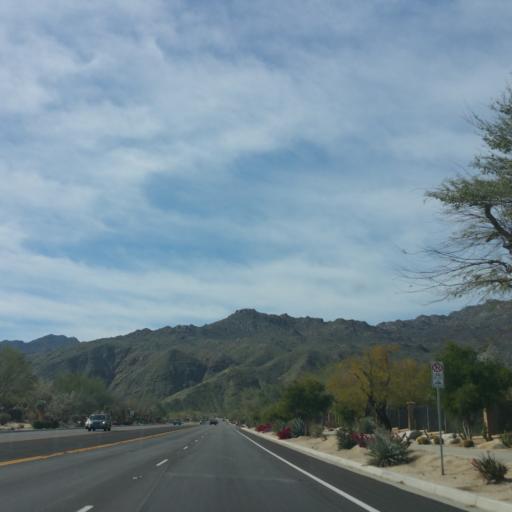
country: US
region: California
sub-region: Riverside County
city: Palm Desert
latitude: 33.6804
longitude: -116.4062
